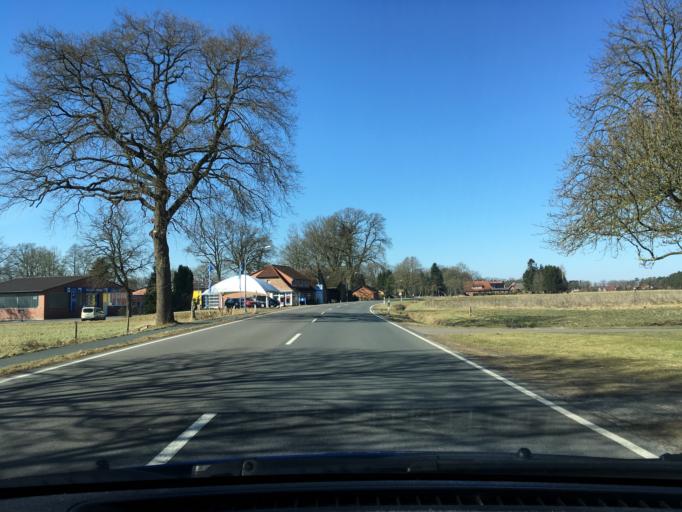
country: DE
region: Lower Saxony
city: Brockel
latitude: 53.0963
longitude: 9.5126
